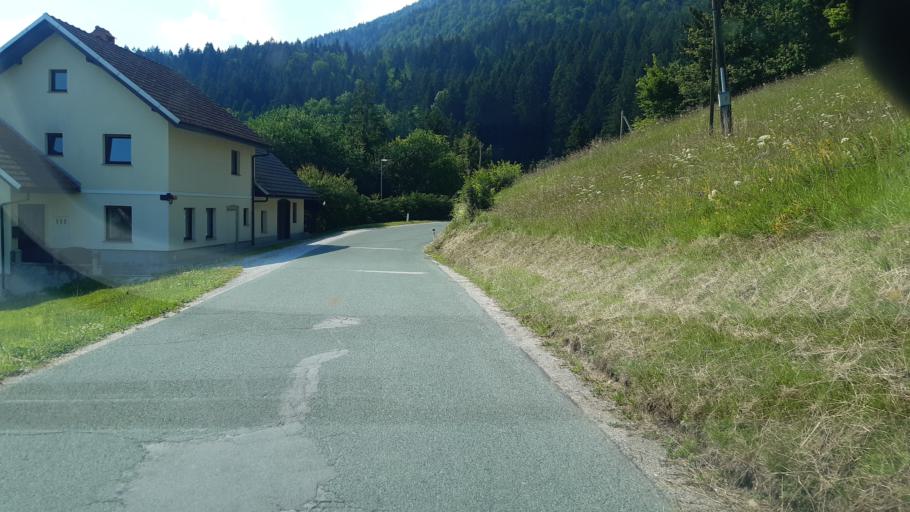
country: SI
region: Trzic
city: Bistrica pri Trzicu
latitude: 46.3596
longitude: 14.2642
